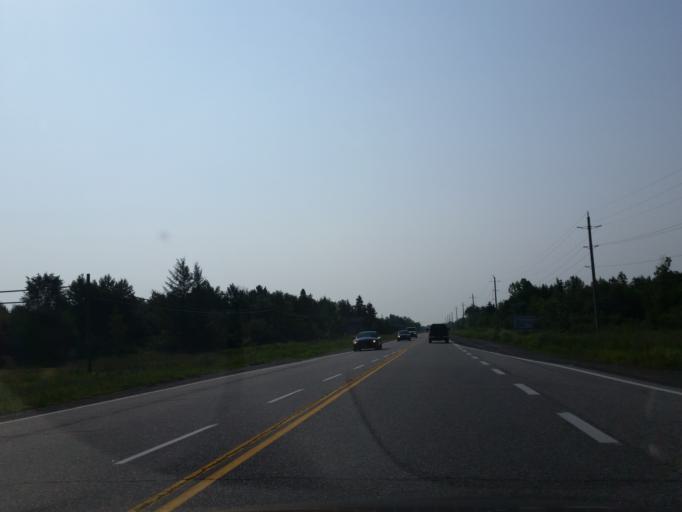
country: CA
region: Ontario
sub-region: Nipissing District
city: North Bay
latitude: 46.3770
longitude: -79.9712
